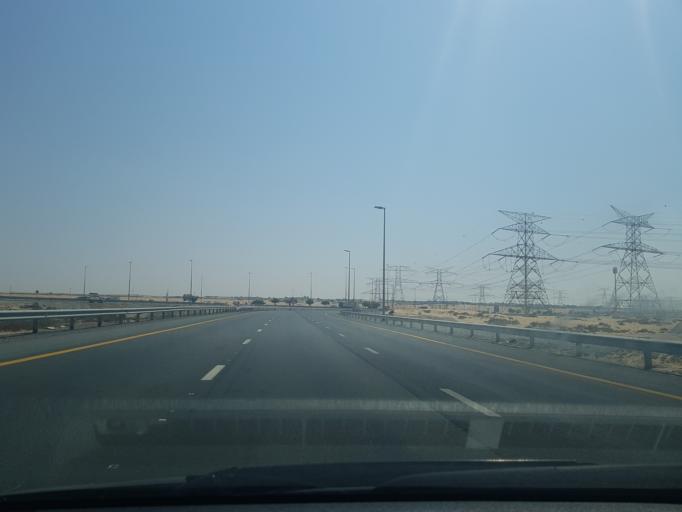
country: AE
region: Ash Shariqah
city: Sharjah
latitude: 25.2371
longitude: 55.5633
